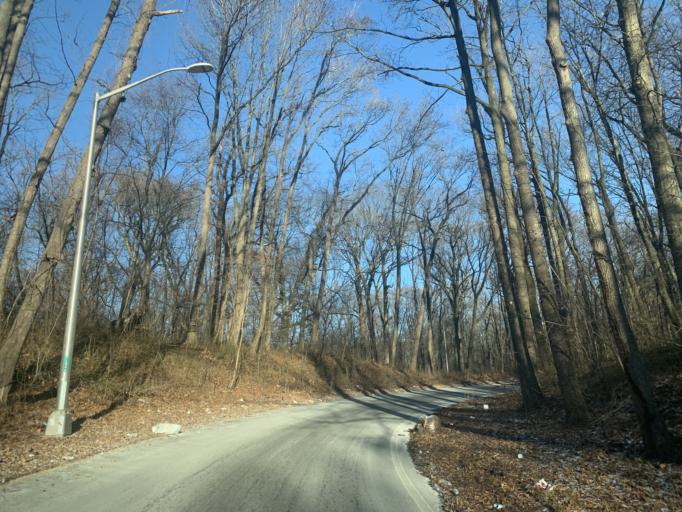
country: US
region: New York
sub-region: Nassau County
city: Bellerose Terrace
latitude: 40.7273
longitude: -73.7665
